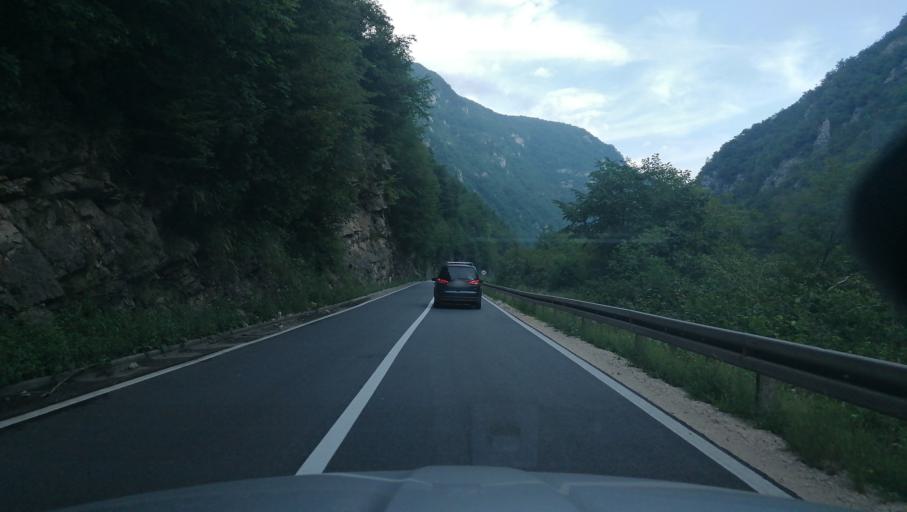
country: BA
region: Federation of Bosnia and Herzegovina
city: Jajce
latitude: 44.4311
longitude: 17.2376
